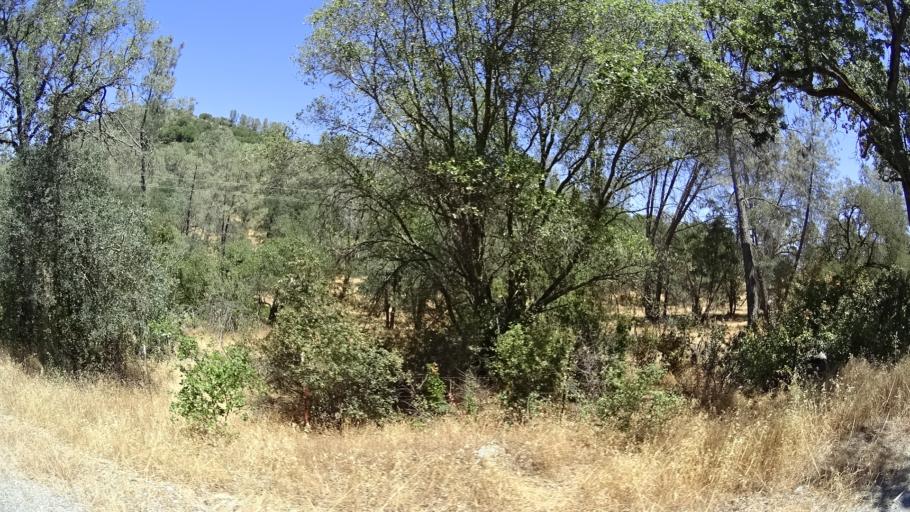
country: US
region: California
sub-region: Calaveras County
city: Copperopolis
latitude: 38.0509
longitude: -120.6500
